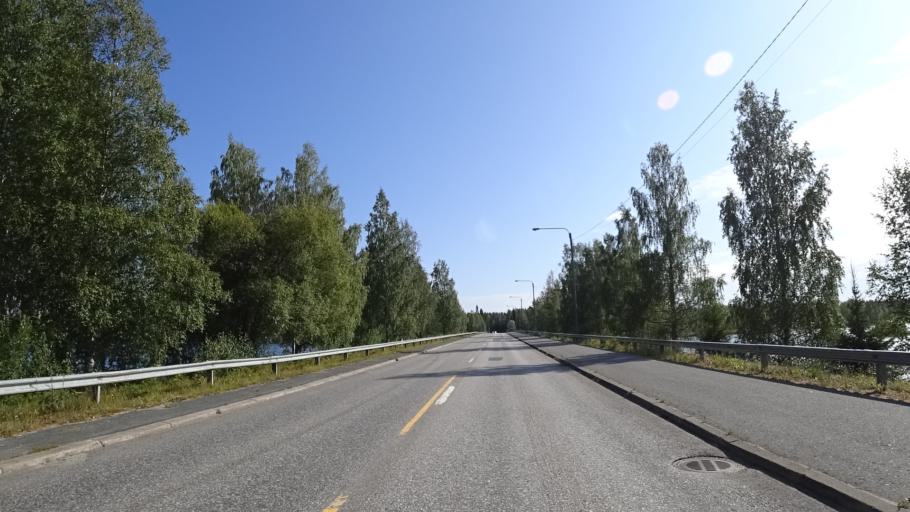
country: FI
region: North Karelia
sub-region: Joensuu
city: Eno
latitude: 62.8056
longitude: 30.1524
